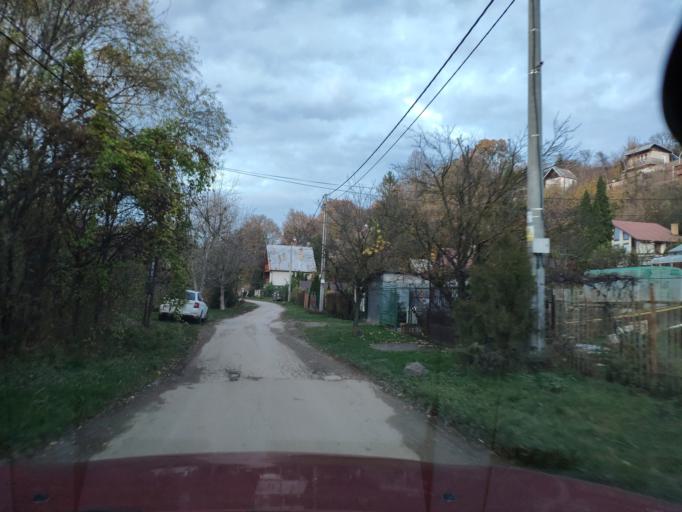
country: SK
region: Kosicky
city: Kosice
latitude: 48.6659
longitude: 21.3557
